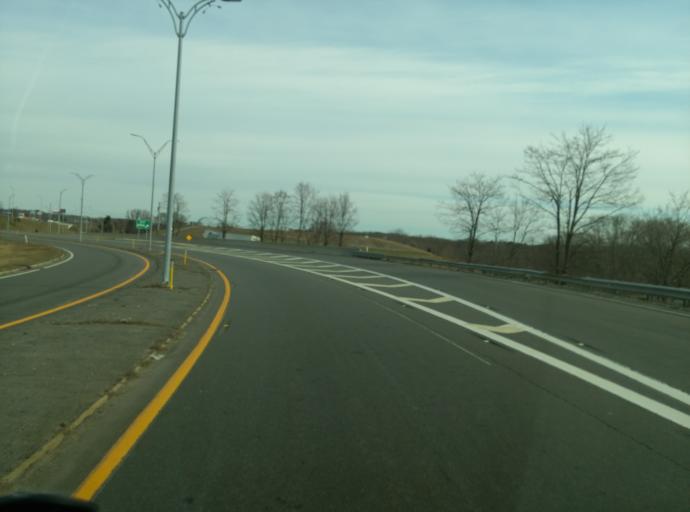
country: US
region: Massachusetts
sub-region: Essex County
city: North Andover
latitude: 42.7099
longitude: -71.1357
